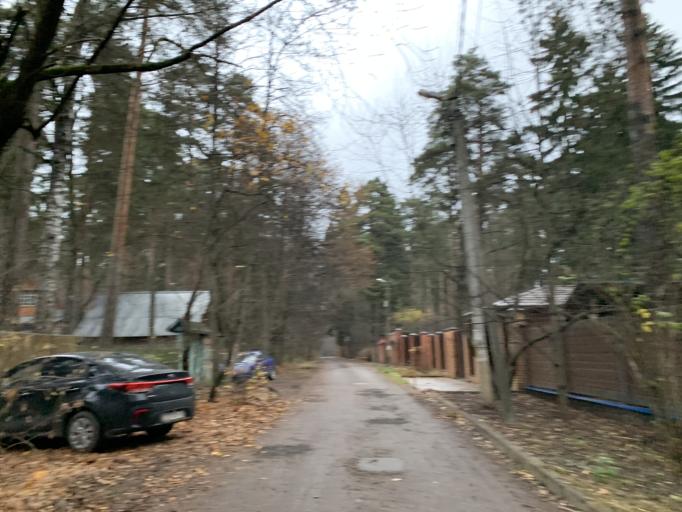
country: RU
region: Moskovskaya
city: Mamontovka
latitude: 55.9857
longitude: 37.8150
